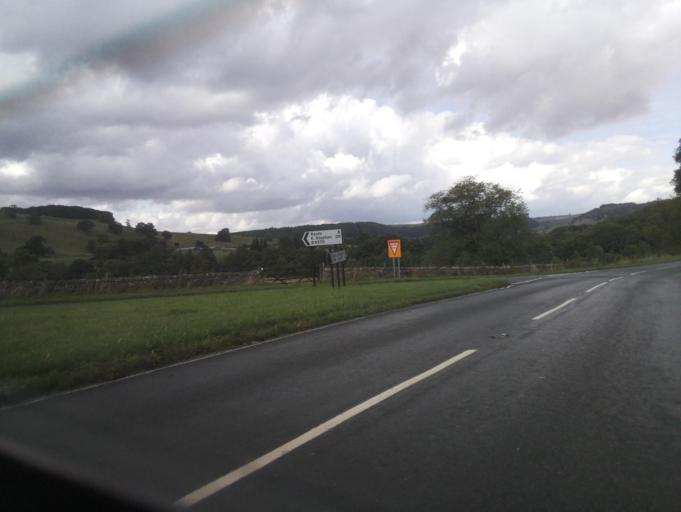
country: GB
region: England
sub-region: North Yorkshire
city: Leyburn
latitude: 54.3854
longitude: -1.8292
